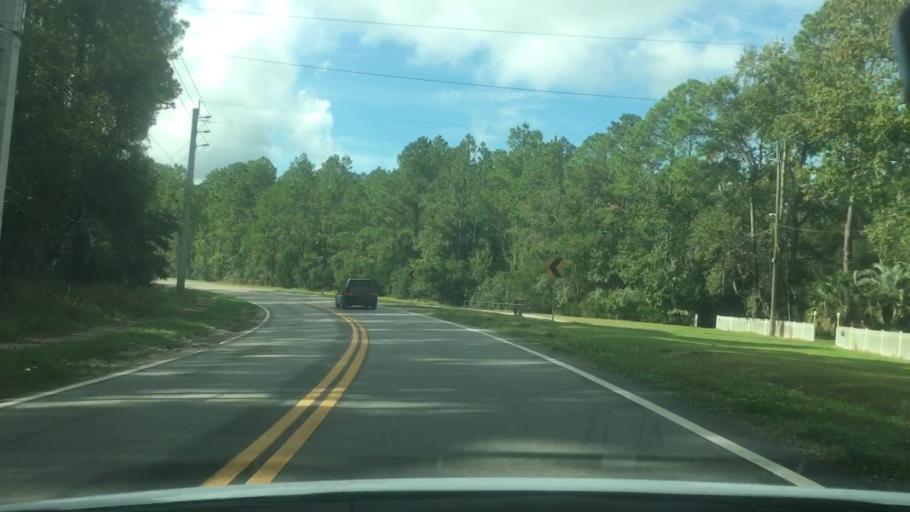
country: US
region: Florida
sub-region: Nassau County
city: Yulee
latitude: 30.4999
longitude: -81.5871
